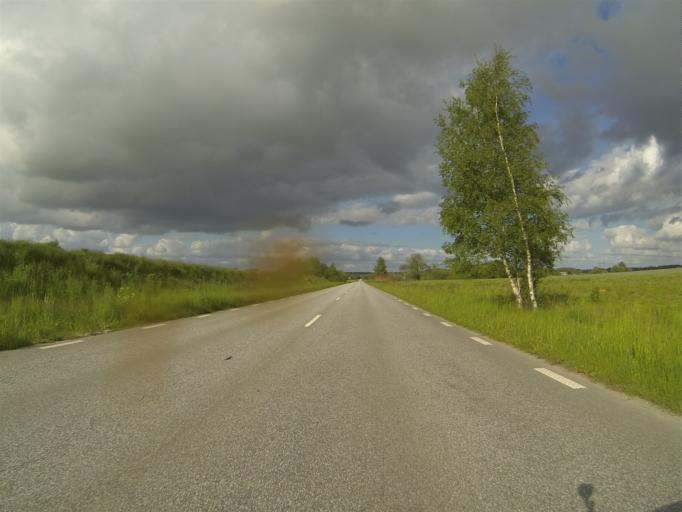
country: SE
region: Skane
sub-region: Lunds Kommun
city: Genarp
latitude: 55.7252
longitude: 13.3700
